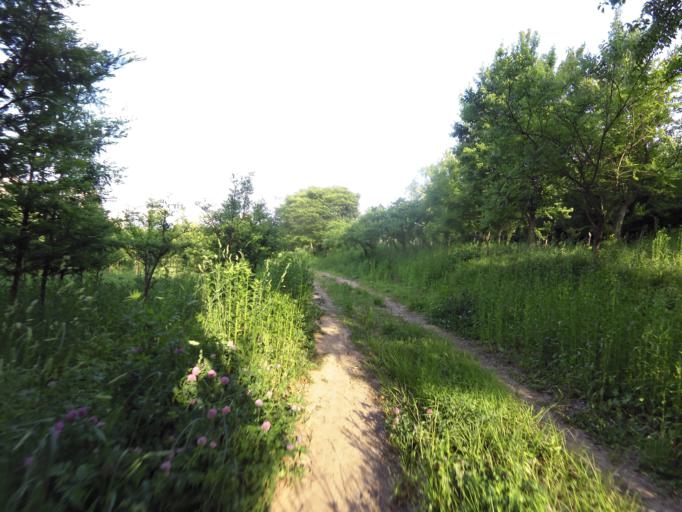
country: KR
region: Gyeongsangbuk-do
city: Gyeongsan-si
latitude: 35.8376
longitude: 128.7618
